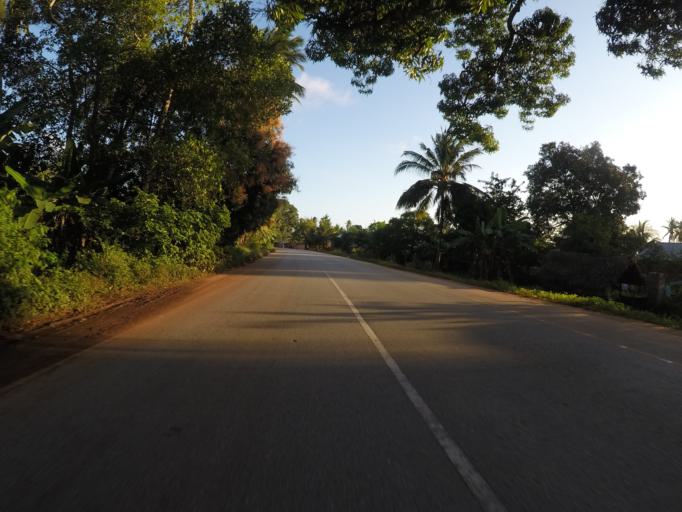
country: TZ
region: Zanzibar North
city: Mkokotoni
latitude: -5.8544
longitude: 39.2818
